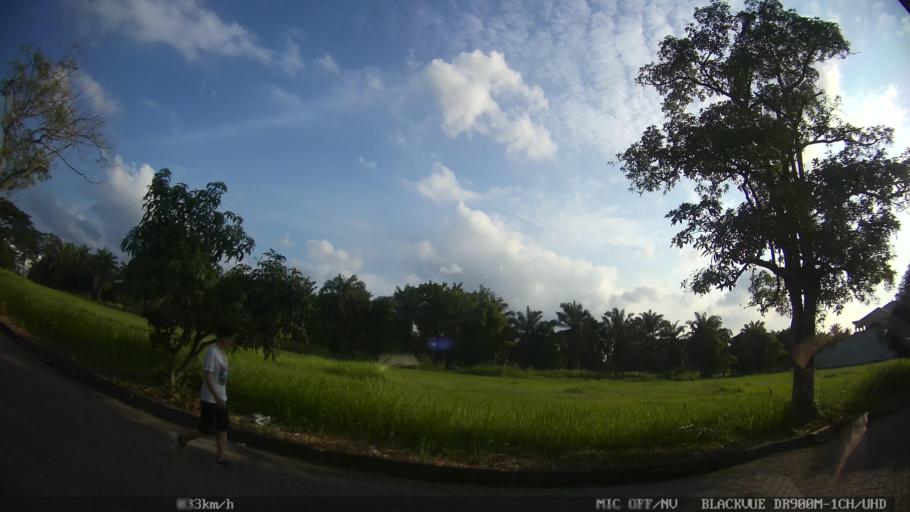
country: ID
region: North Sumatra
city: Medan
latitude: 3.6240
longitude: 98.6572
